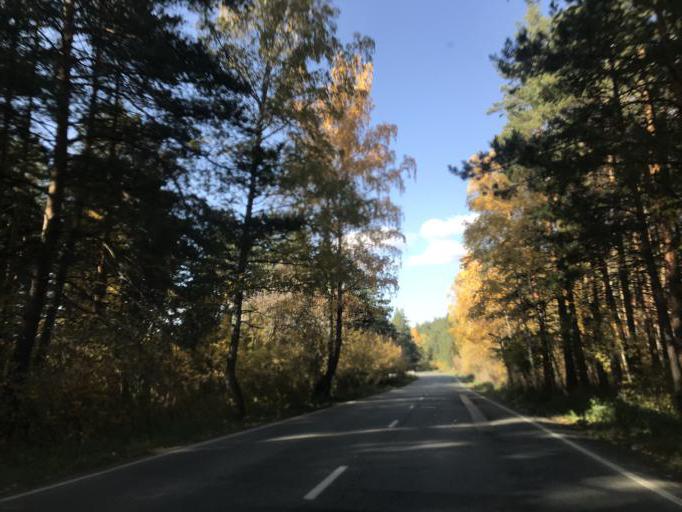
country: RU
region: Chelyabinsk
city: Dolgoderevenskoye
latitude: 55.2855
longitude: 61.3586
